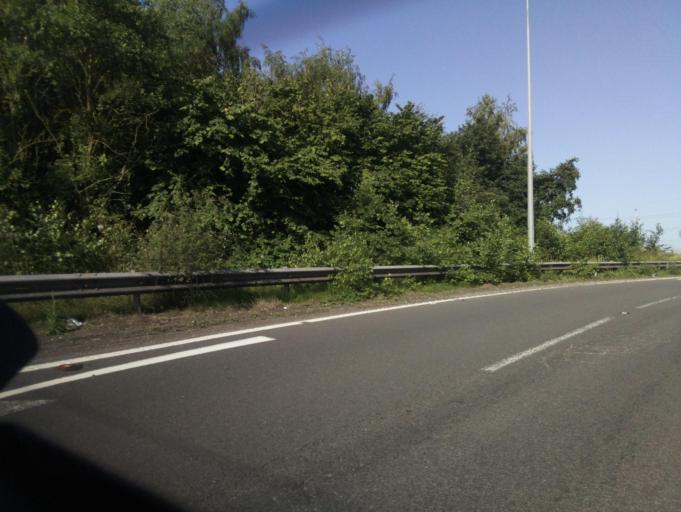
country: GB
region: England
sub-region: Staffordshire
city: Shenstone
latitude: 52.6509
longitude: -1.8333
